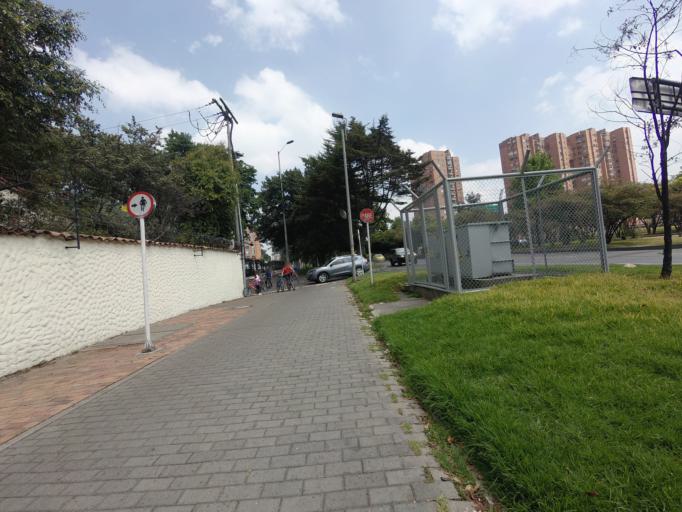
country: CO
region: Bogota D.C.
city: Barrio San Luis
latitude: 4.7167
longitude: -74.0761
